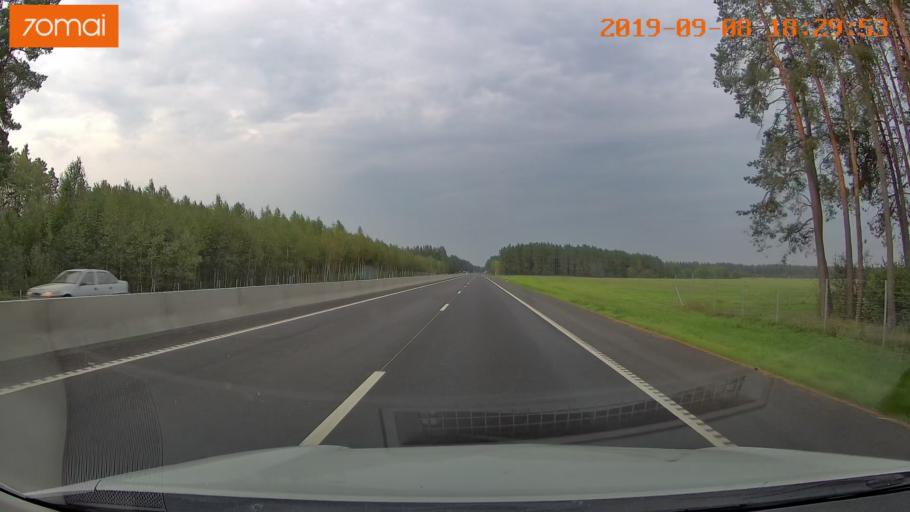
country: BY
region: Grodnenskaya
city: Iwye
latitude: 53.8687
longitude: 25.6514
